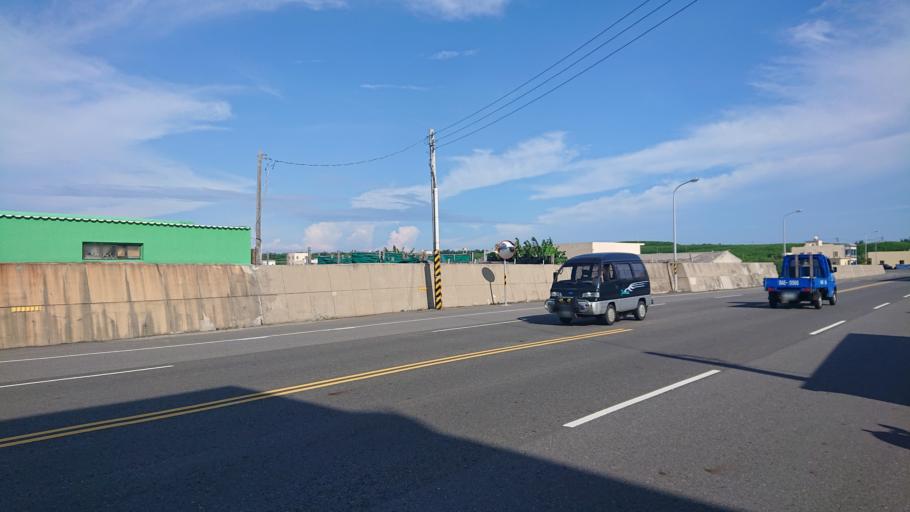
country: TW
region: Taiwan
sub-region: Penghu
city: Ma-kung
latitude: 23.5214
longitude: 119.5733
